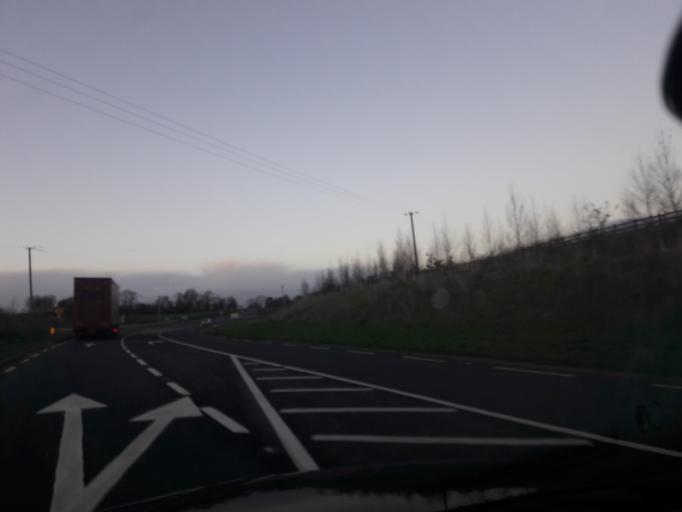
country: IE
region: Ulster
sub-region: County Monaghan
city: Monaghan
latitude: 54.2848
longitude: -6.9674
